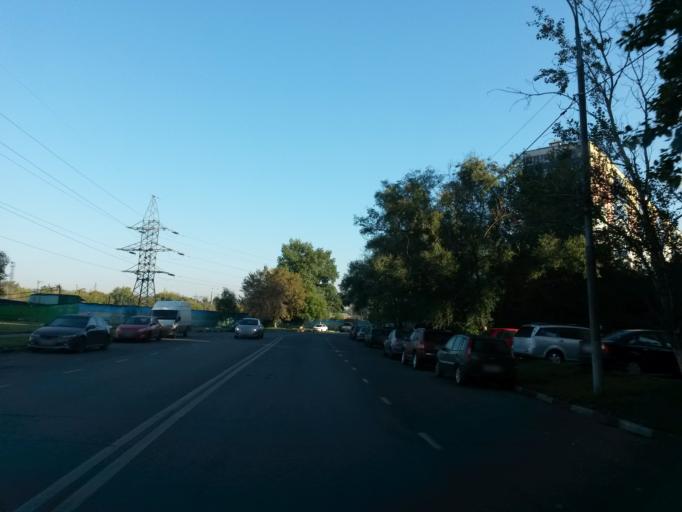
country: RU
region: Moskovskaya
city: Kur'yanovo
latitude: 55.6495
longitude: 37.7083
